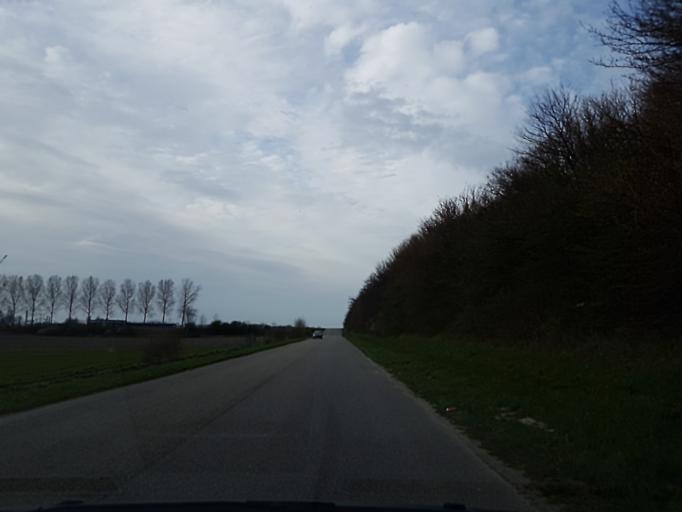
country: NL
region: Zeeland
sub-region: Gemeente Terneuzen
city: Terneuzen
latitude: 51.3333
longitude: 3.8096
